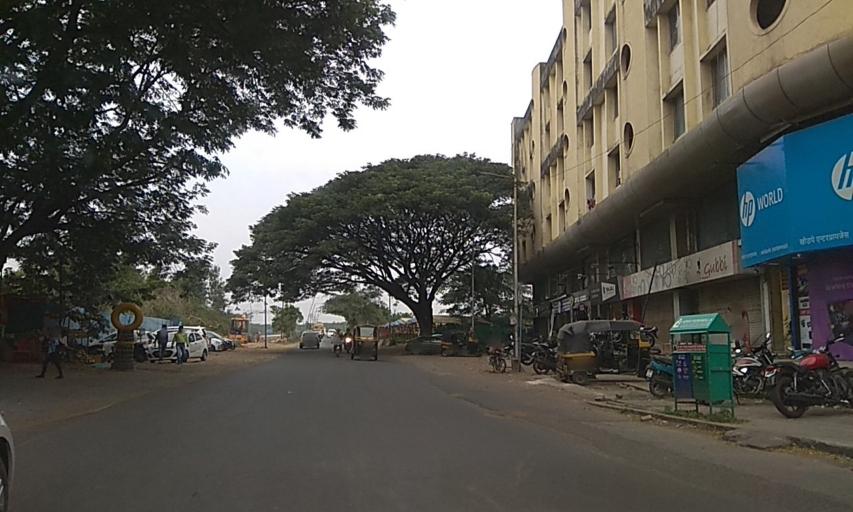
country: IN
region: Maharashtra
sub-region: Pune Division
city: Khadki
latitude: 18.5667
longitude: 73.8075
